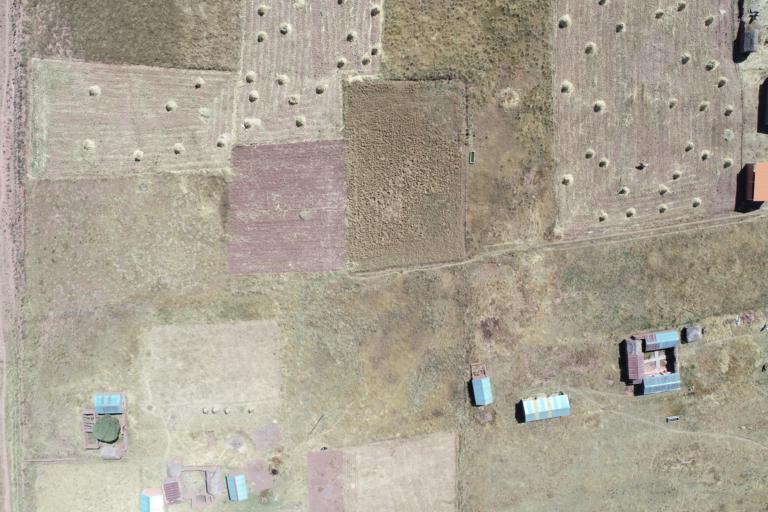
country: BO
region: La Paz
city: Tiahuanaco
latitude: -16.5911
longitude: -68.7538
